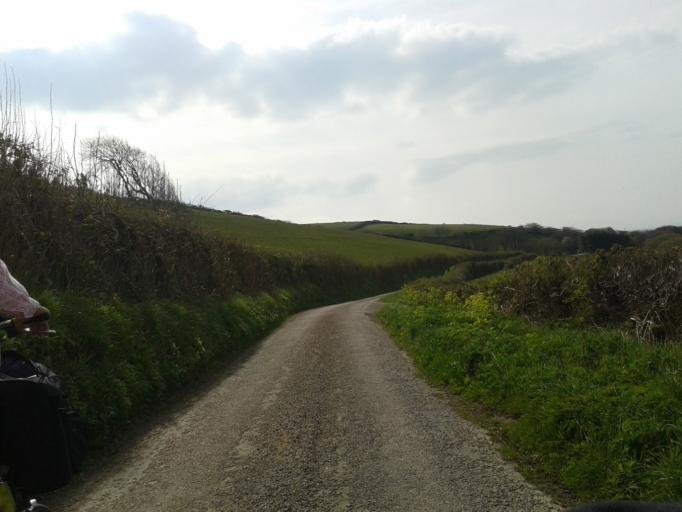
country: GB
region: England
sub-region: Devon
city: Braunton
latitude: 51.1300
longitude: -4.2005
